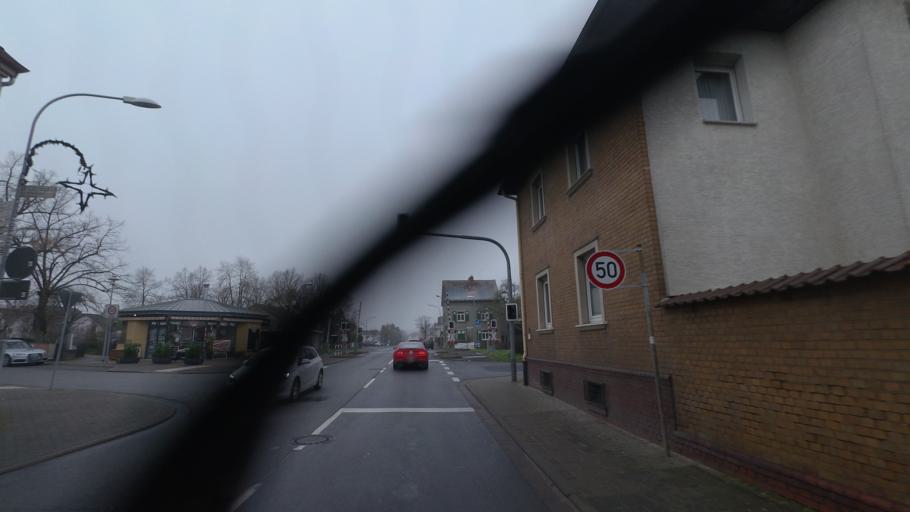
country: DE
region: Hesse
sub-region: Regierungsbezirk Darmstadt
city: Grosskrotzenburg
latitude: 50.0798
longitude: 8.9372
